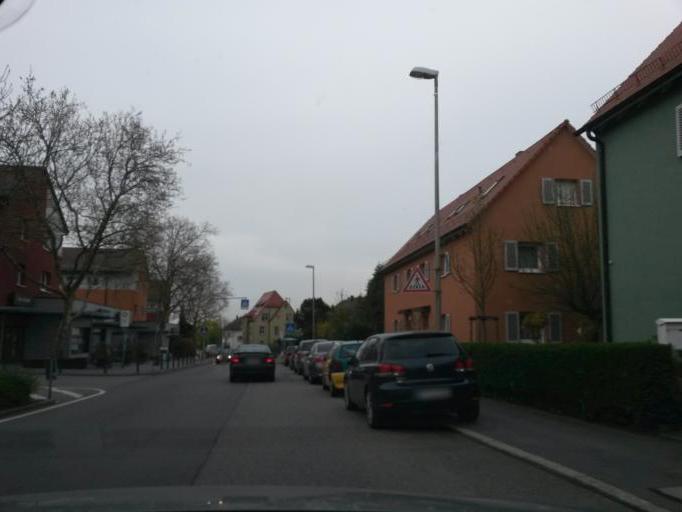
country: DE
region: Baden-Wuerttemberg
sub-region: Karlsruhe Region
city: Ispringen
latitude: 48.8867
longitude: 8.6593
